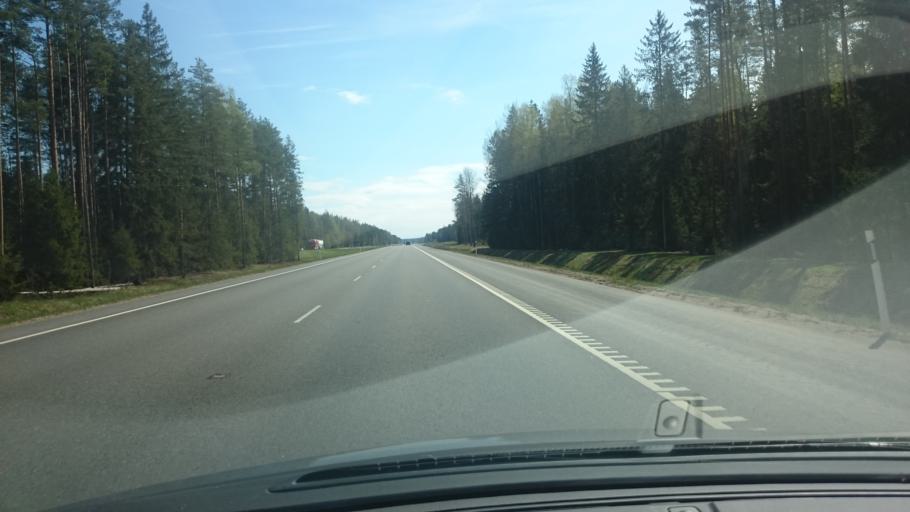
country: EE
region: Harju
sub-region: Loksa linn
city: Loksa
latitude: 59.4570
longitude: 25.8559
